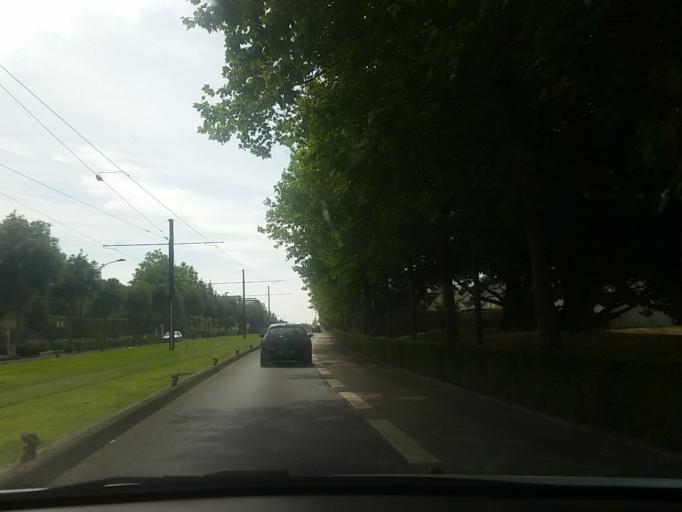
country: FR
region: Pays de la Loire
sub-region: Departement de la Loire-Atlantique
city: Saint-Herblain
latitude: 47.2168
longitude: -1.6117
